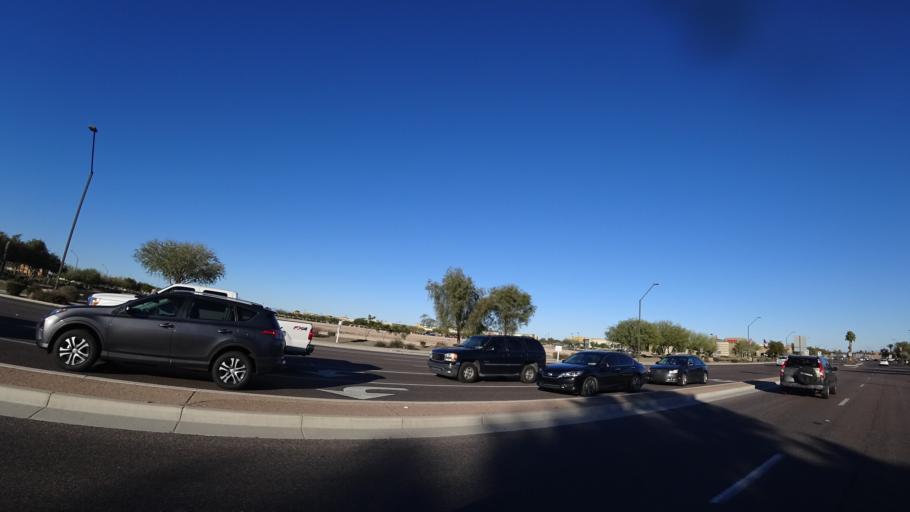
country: US
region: Arizona
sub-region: Maricopa County
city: Litchfield Park
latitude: 33.4645
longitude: -112.3918
